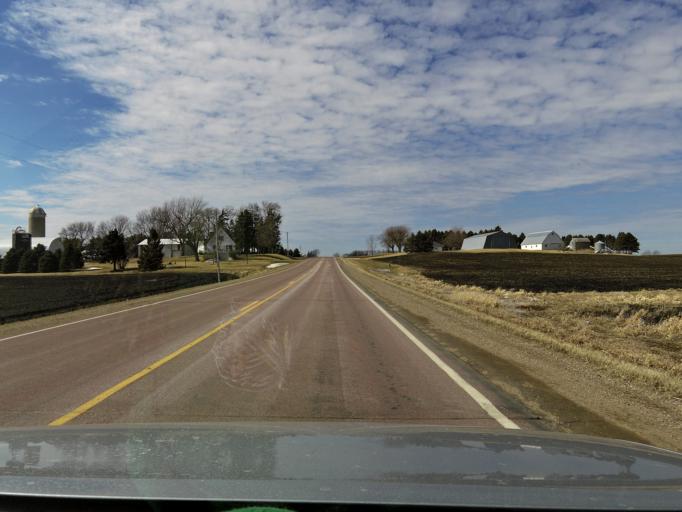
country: US
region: Minnesota
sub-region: Le Sueur County
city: Montgomery
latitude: 44.4859
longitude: -93.6494
